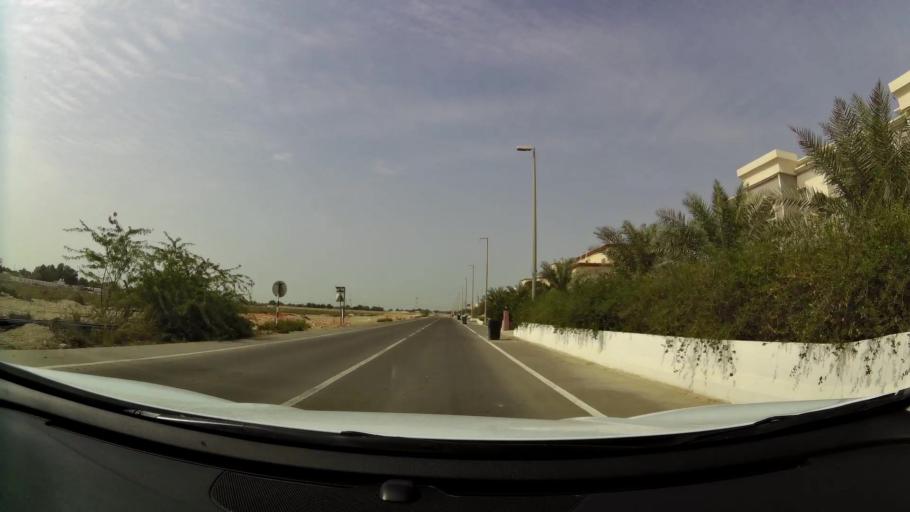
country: AE
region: Abu Dhabi
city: Abu Dhabi
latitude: 24.5419
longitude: 54.6655
